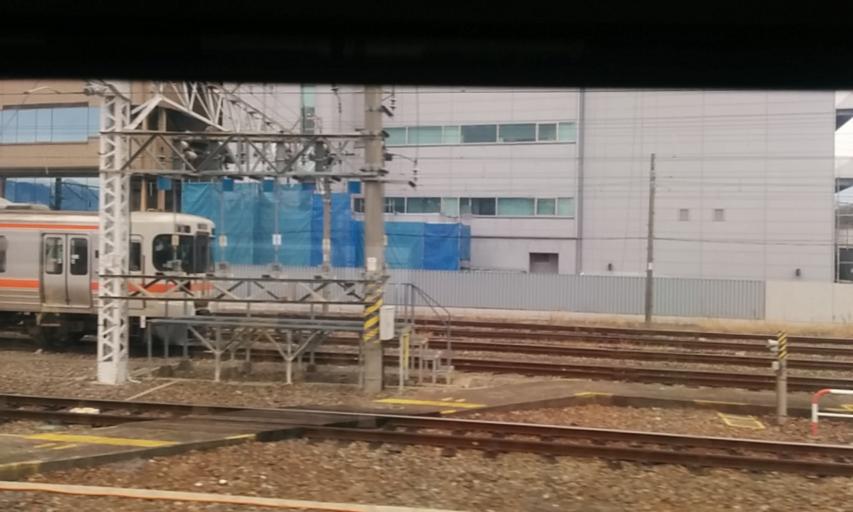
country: JP
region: Nagano
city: Matsumoto
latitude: 36.2282
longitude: 137.9659
